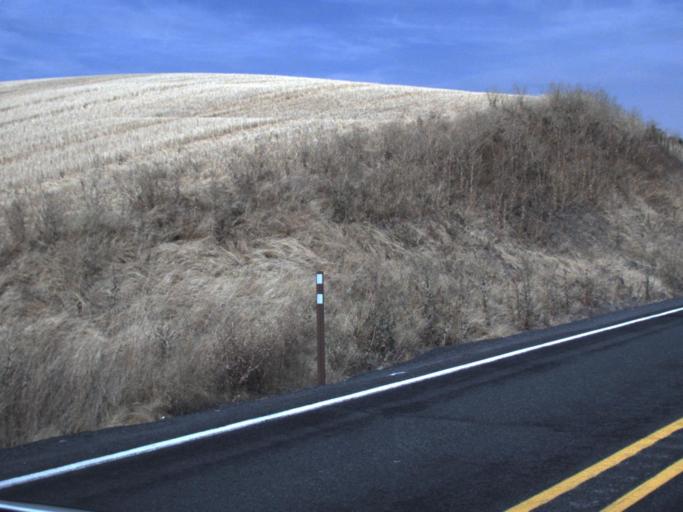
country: US
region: Washington
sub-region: Whitman County
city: Pullman
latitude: 46.9612
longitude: -117.0913
